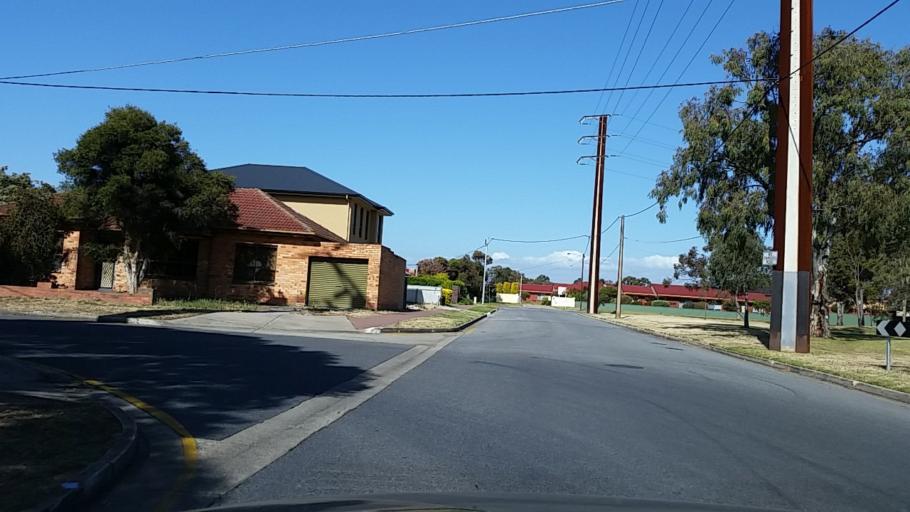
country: AU
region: South Australia
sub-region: Charles Sturt
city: Henley Beach
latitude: -34.9170
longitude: 138.5048
